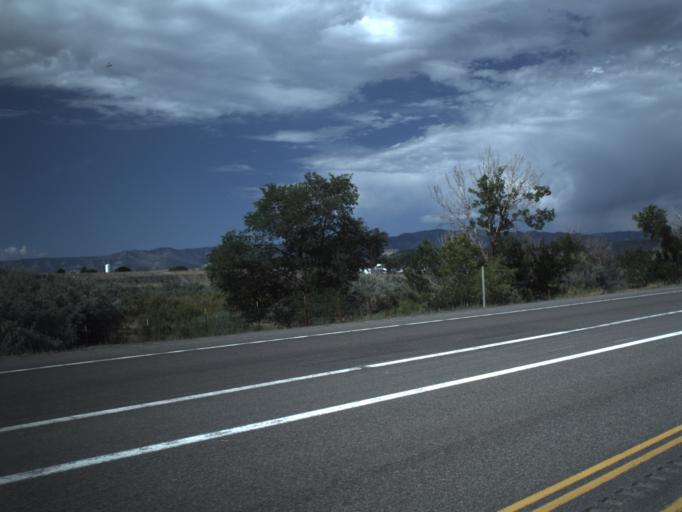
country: US
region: Utah
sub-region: Carbon County
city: Price
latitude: 39.5856
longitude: -110.8055
